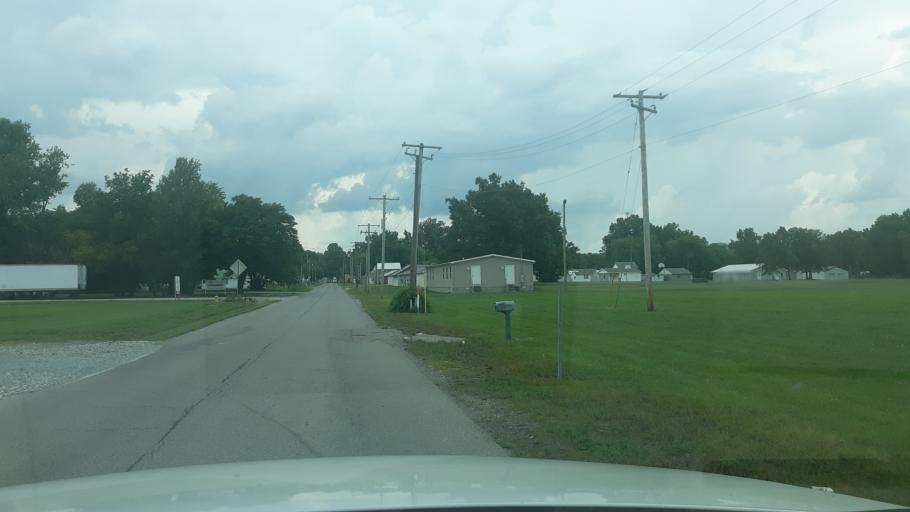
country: US
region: Illinois
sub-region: Saline County
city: Eldorado
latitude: 37.8034
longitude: -88.4566
